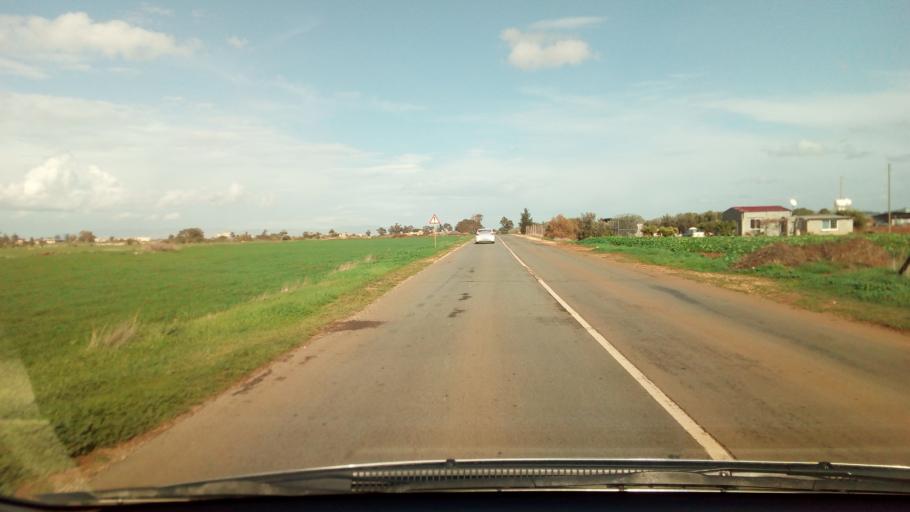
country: CY
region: Ammochostos
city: Achna
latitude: 35.0504
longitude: 33.7924
